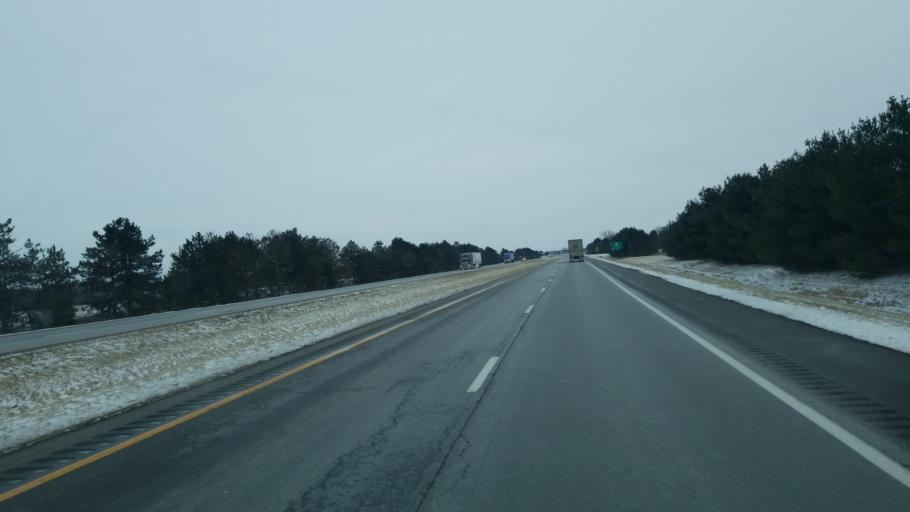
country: US
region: Ohio
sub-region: Wyandot County
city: Carey
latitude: 40.9786
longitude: -83.4944
